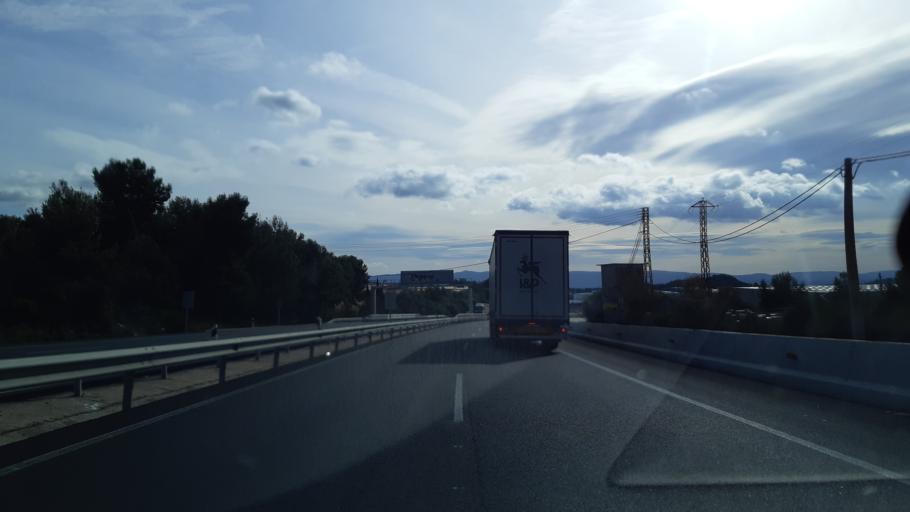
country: ES
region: Catalonia
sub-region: Provincia de Barcelona
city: Collbato
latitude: 41.5814
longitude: 1.7775
